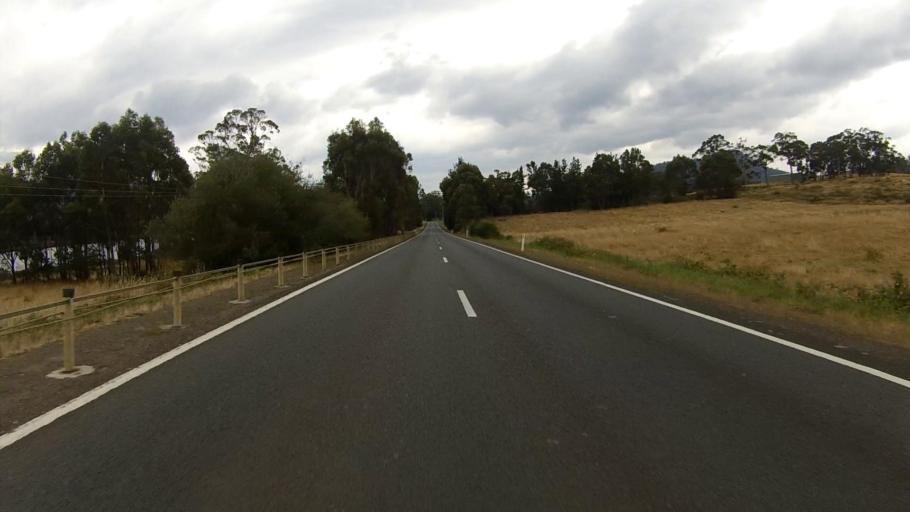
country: AU
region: Tasmania
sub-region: Huon Valley
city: Franklin
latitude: -43.0824
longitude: 147.0309
